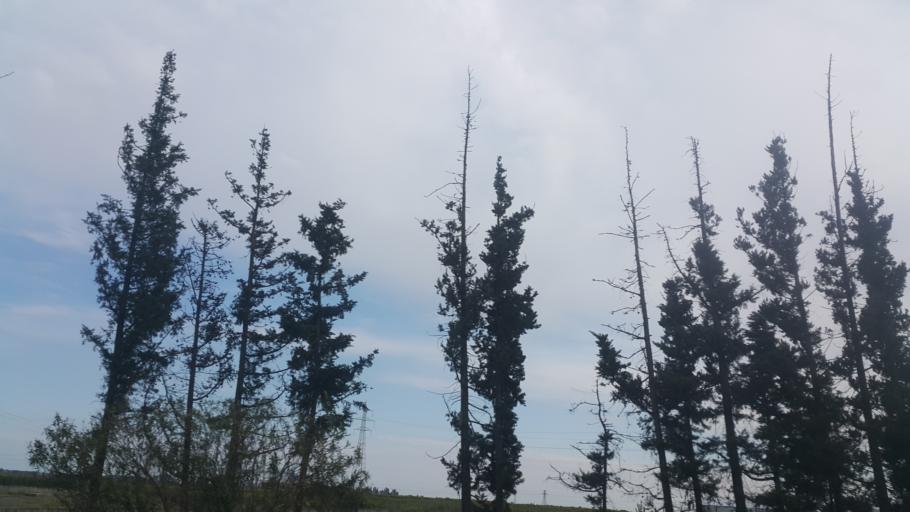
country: TR
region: Mersin
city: Yenice
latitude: 36.9853
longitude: 35.1245
